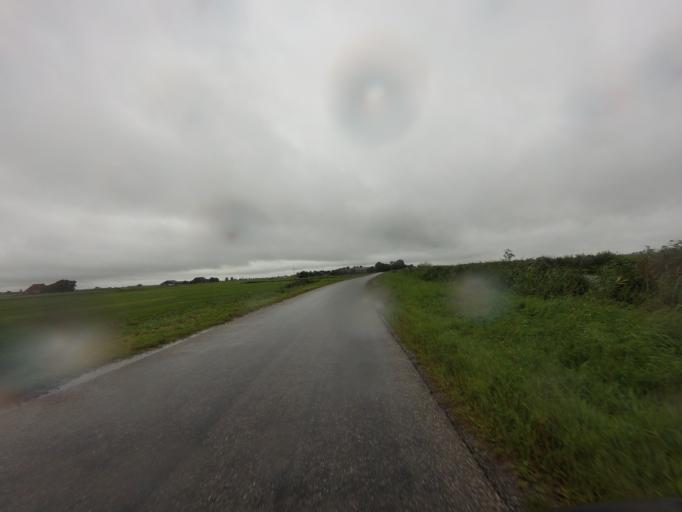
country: NL
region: Friesland
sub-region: Sudwest Fryslan
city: Workum
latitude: 53.0046
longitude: 5.4726
